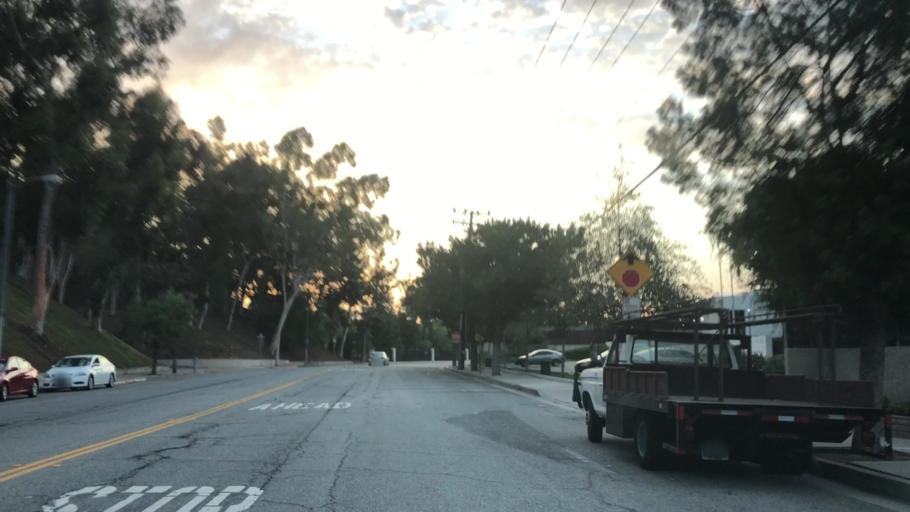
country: US
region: California
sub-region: Los Angeles County
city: South San Gabriel
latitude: 34.0428
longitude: -118.0938
